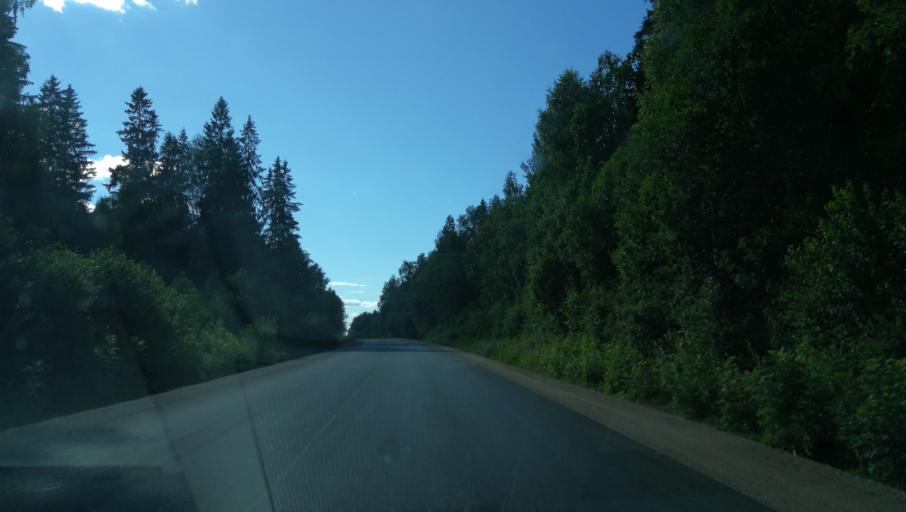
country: LV
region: Vecpiebalga
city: Vecpiebalga
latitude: 57.0537
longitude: 25.8790
